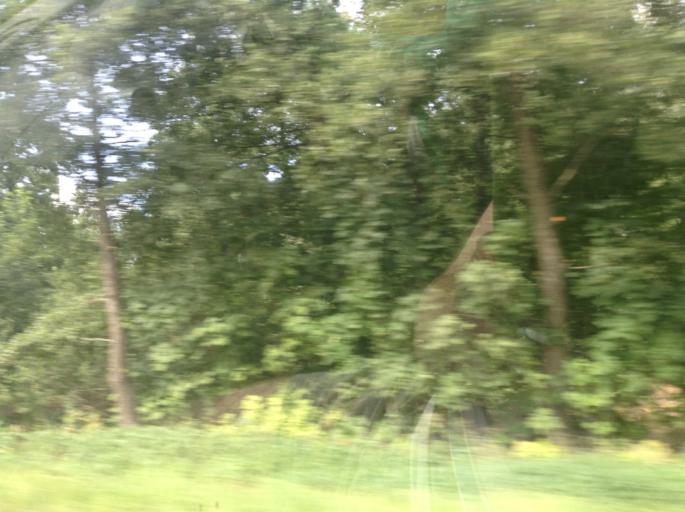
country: RU
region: Moskovskaya
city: Yegor'yevsk
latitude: 55.3592
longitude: 39.1118
